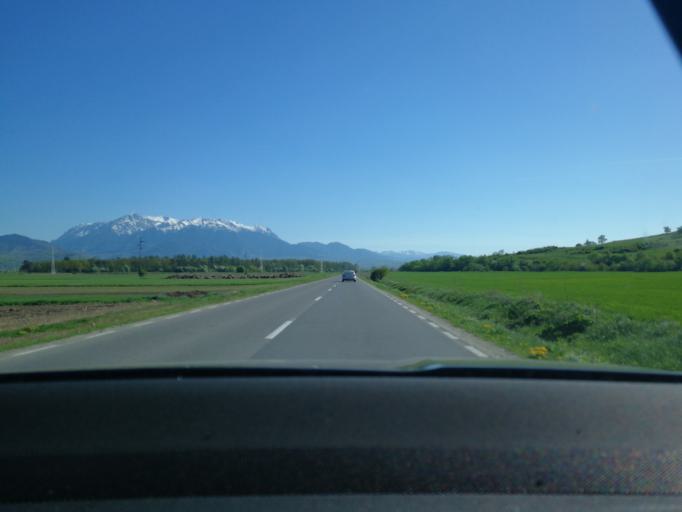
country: RO
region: Brasov
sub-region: Comuna Vulcan
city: Vulcan
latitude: 45.6055
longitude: 25.4213
